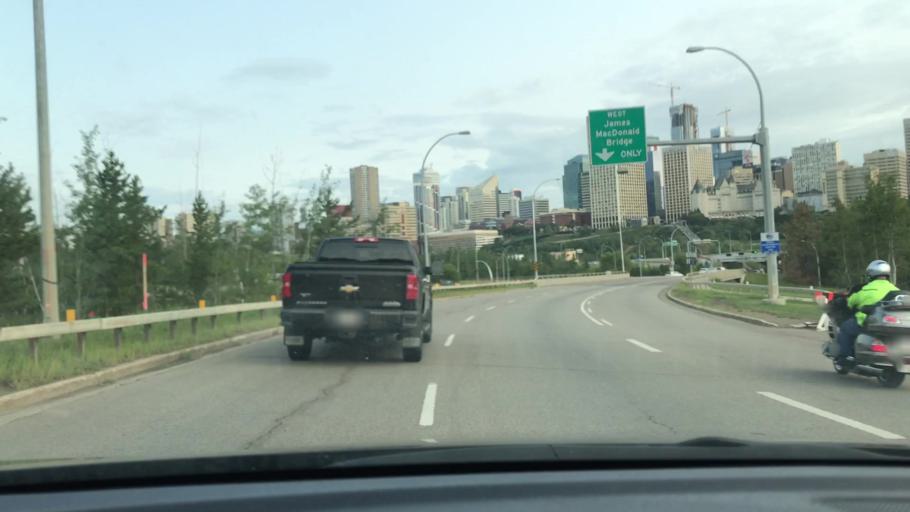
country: CA
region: Alberta
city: Edmonton
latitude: 53.5332
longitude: -113.4815
